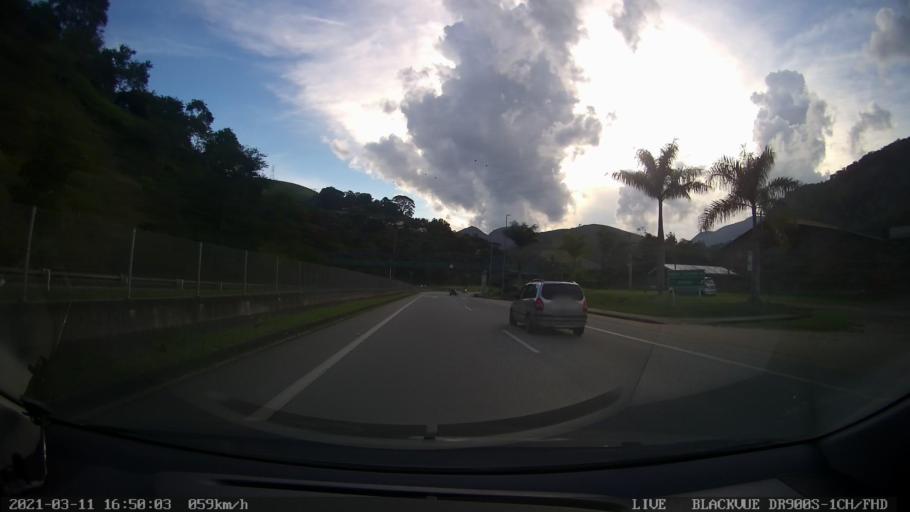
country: BR
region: Rio de Janeiro
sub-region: Petropolis
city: Petropolis
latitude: -22.4270
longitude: -43.1588
